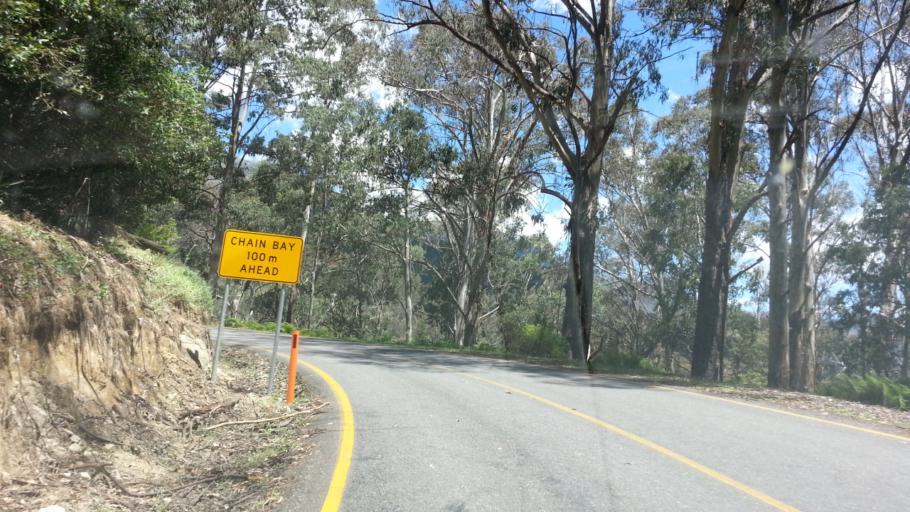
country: AU
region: Victoria
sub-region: Alpine
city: Mount Beauty
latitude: -36.8449
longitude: 147.2395
